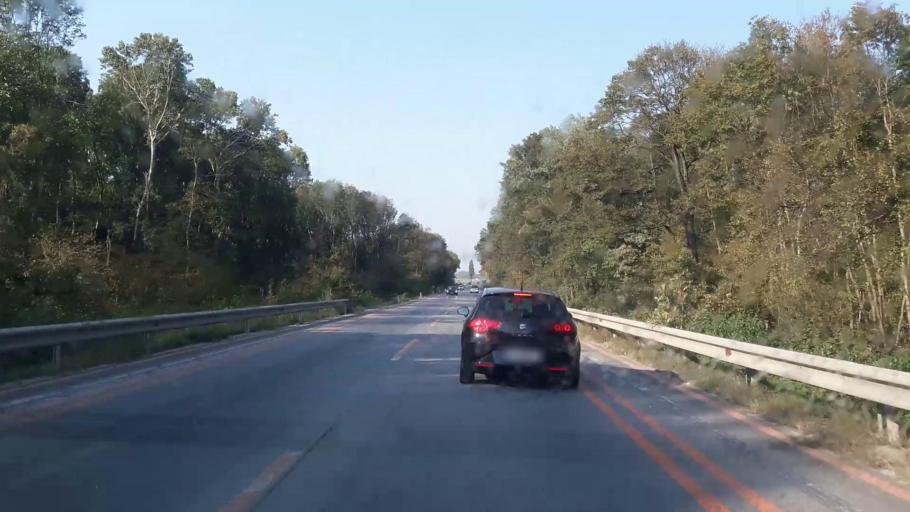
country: AT
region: Lower Austria
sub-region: Politischer Bezirk Ganserndorf
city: Engelhartstetten
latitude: 48.1579
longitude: 16.9001
